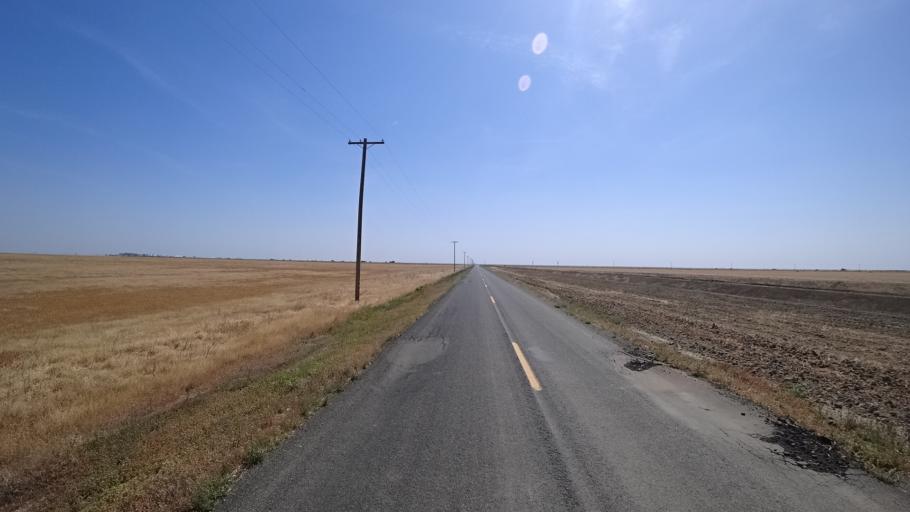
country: US
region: California
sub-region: Kings County
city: Kettleman City
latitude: 36.0941
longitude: -119.9185
